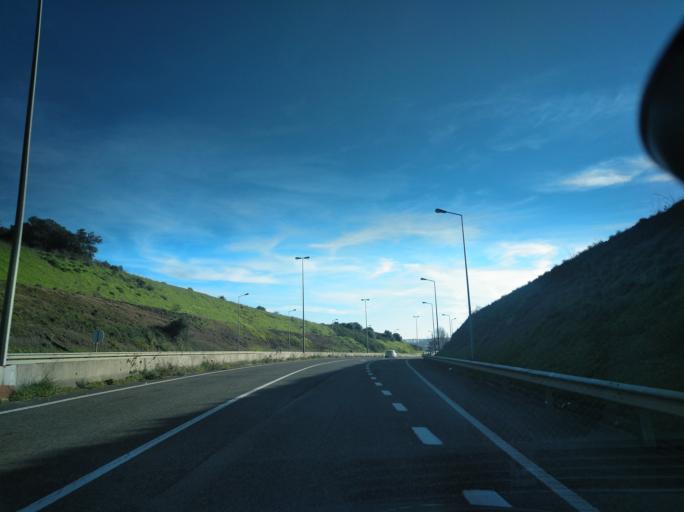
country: PT
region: Lisbon
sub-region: Sintra
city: Pero Pinheiro
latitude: 38.8447
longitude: -9.3493
